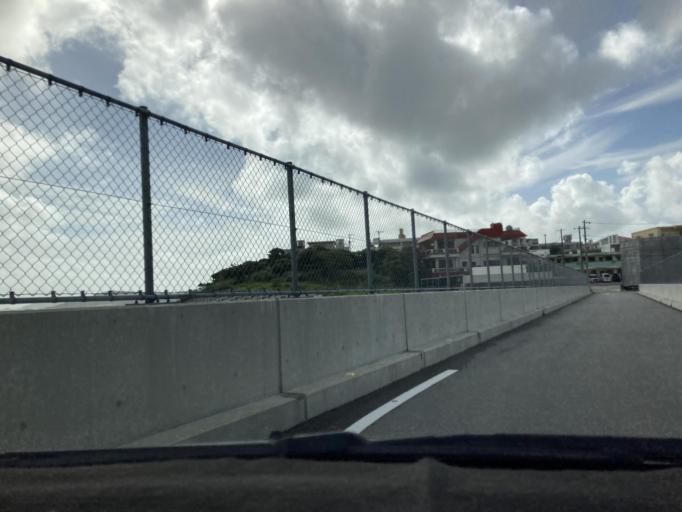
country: JP
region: Okinawa
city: Naha-shi
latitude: 26.2062
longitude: 127.7286
